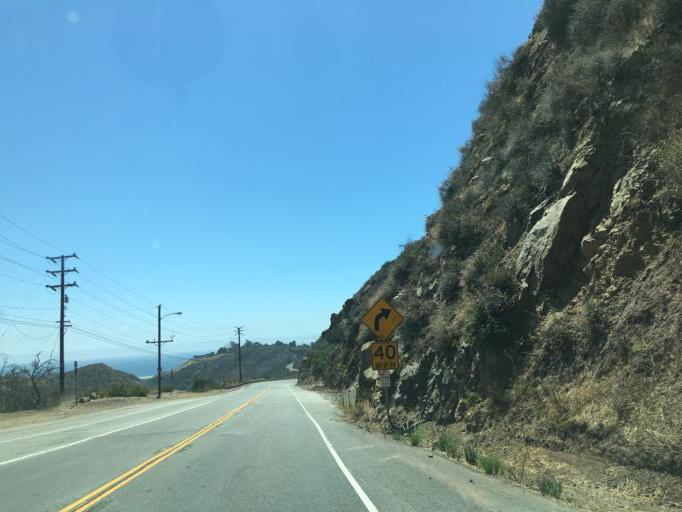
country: US
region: California
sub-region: Los Angeles County
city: Malibu Beach
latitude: 34.0587
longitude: -118.6943
